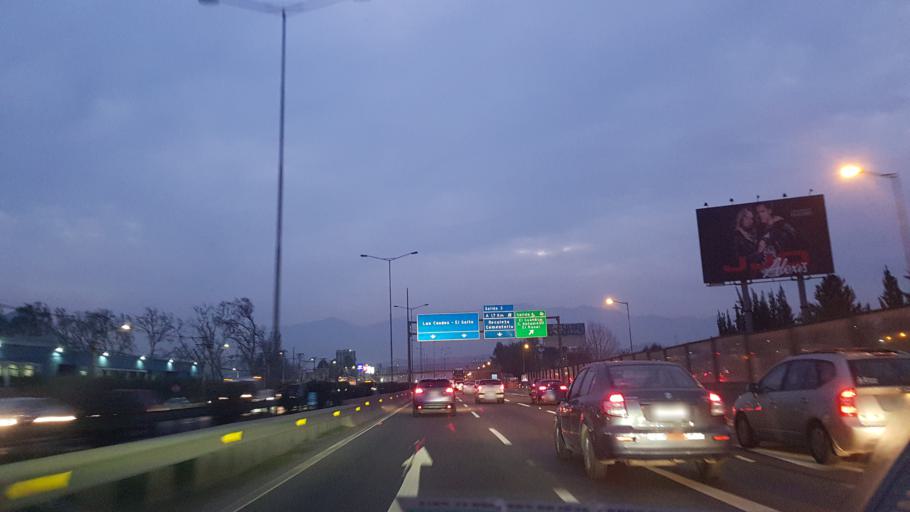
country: CL
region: Santiago Metropolitan
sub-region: Provincia de Santiago
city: Santiago
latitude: -33.3738
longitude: -70.6640
